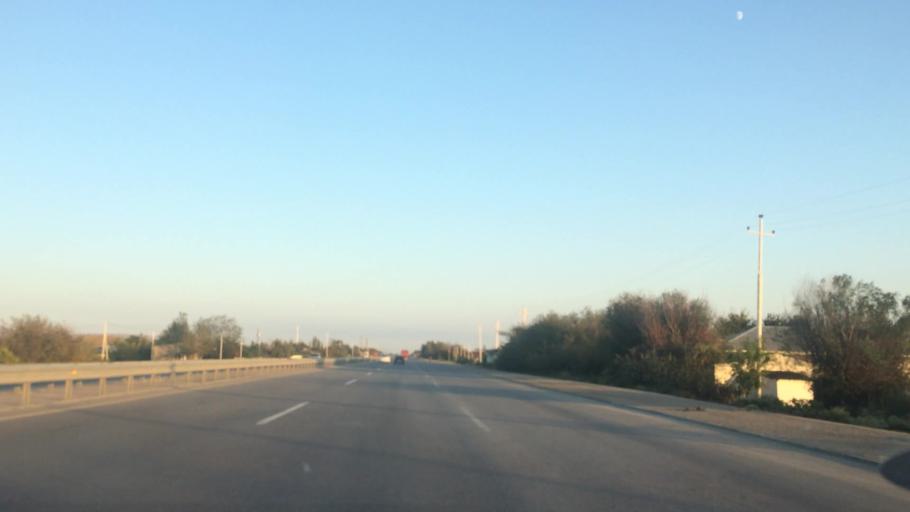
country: AZ
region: Haciqabul
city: Haciqabul
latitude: 40.0176
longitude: 49.1327
